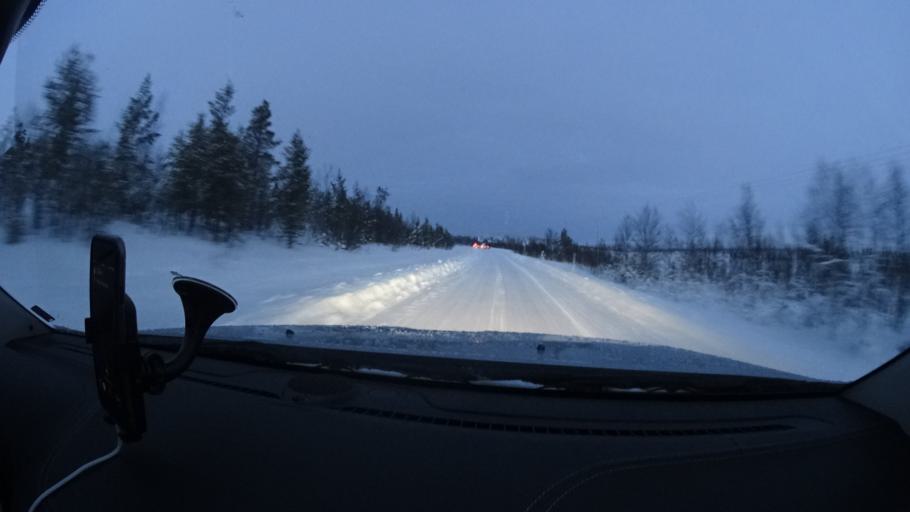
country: FI
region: Lapland
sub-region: Pohjois-Lappi
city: Inari
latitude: 68.5726
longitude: 26.2138
